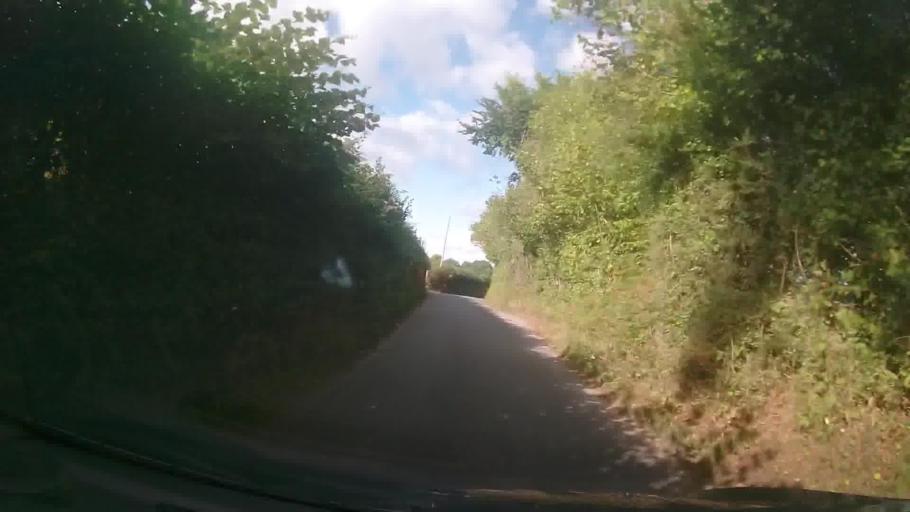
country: GB
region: Wales
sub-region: Sir Powys
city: Brecon
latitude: 51.8875
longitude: -3.3019
